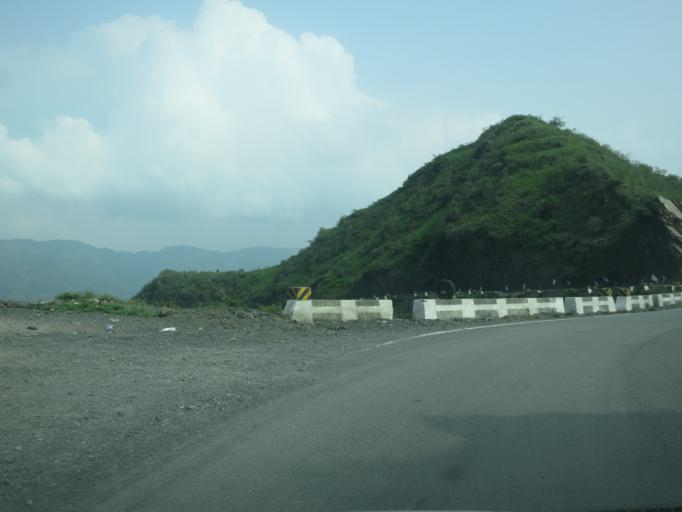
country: IN
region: Himachal Pradesh
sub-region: Solan
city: Arki
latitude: 31.1694
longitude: 76.9973
